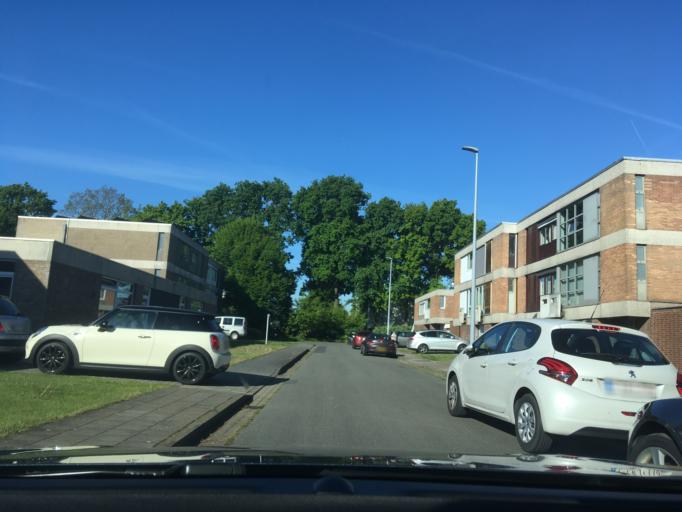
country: BE
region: Flanders
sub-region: Provincie West-Vlaanderen
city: Oostkamp
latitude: 51.1728
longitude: 3.2157
